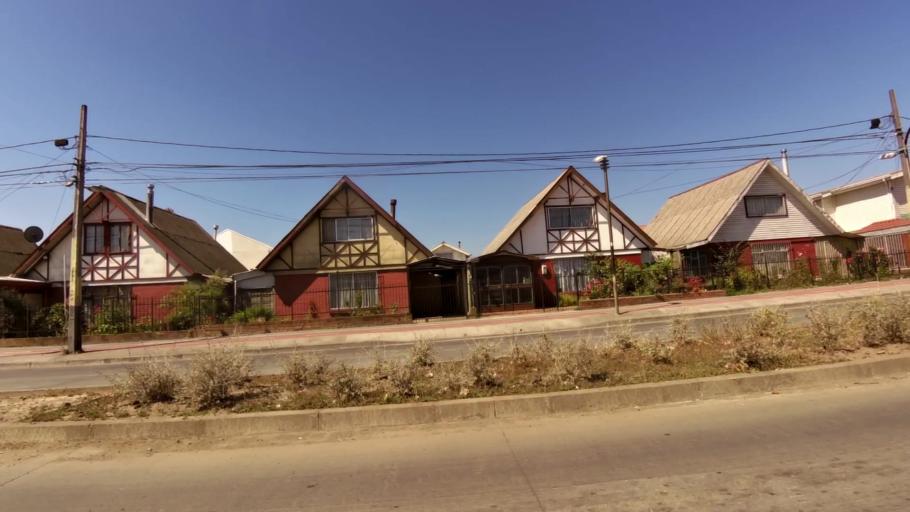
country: CL
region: Biobio
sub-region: Provincia de Concepcion
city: Concepcion
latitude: -36.7951
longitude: -73.0344
